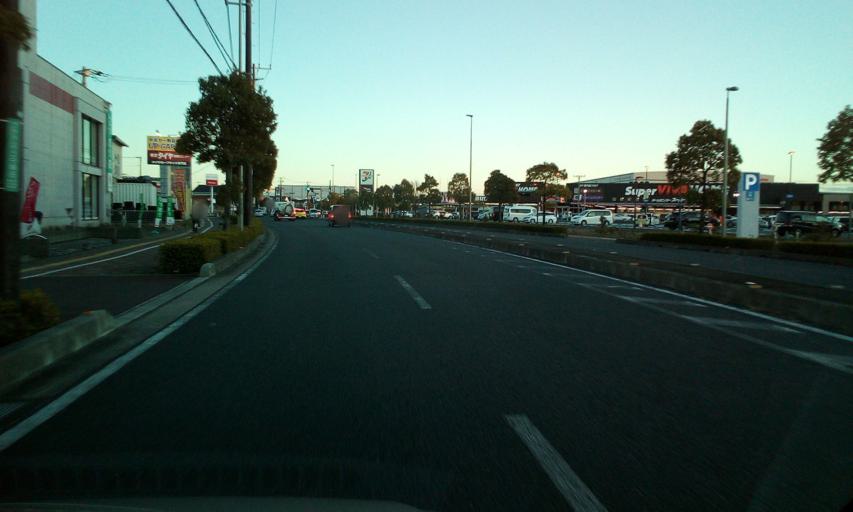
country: JP
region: Saitama
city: Yashio-shi
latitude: 35.8441
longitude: 139.8559
